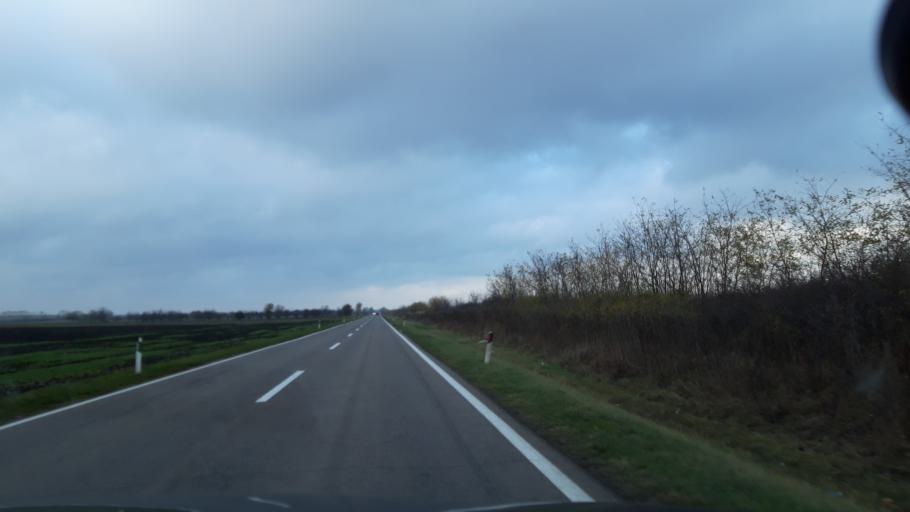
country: RS
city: Sanad
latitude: 46.0091
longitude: 20.0996
